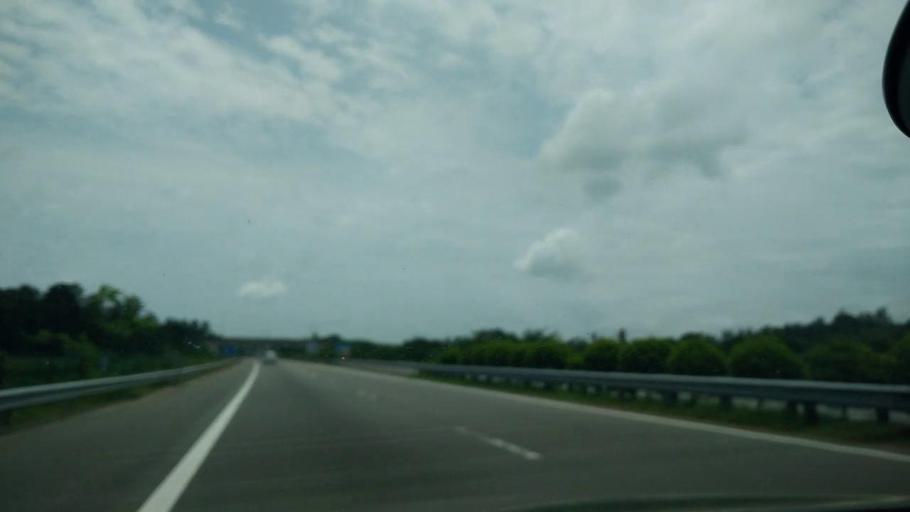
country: LK
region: Western
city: Homagama
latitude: 6.8489
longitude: 79.9787
